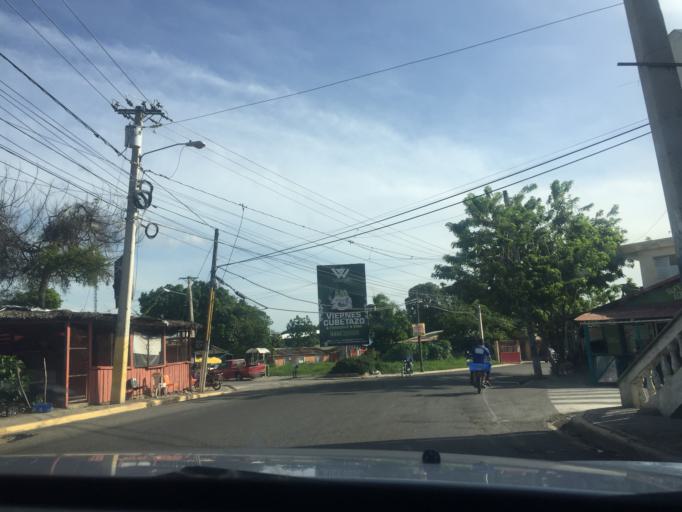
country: DO
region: Santiago
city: Tamboril
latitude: 19.4707
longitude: -70.6462
